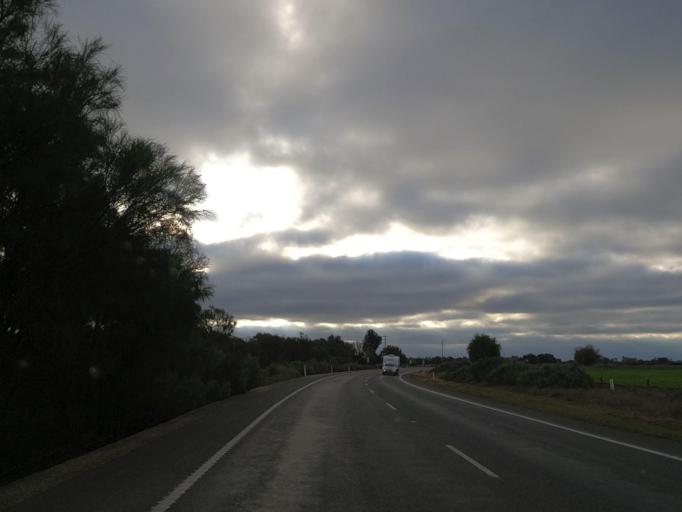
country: AU
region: Victoria
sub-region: Swan Hill
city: Swan Hill
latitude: -35.7218
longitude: 143.8877
